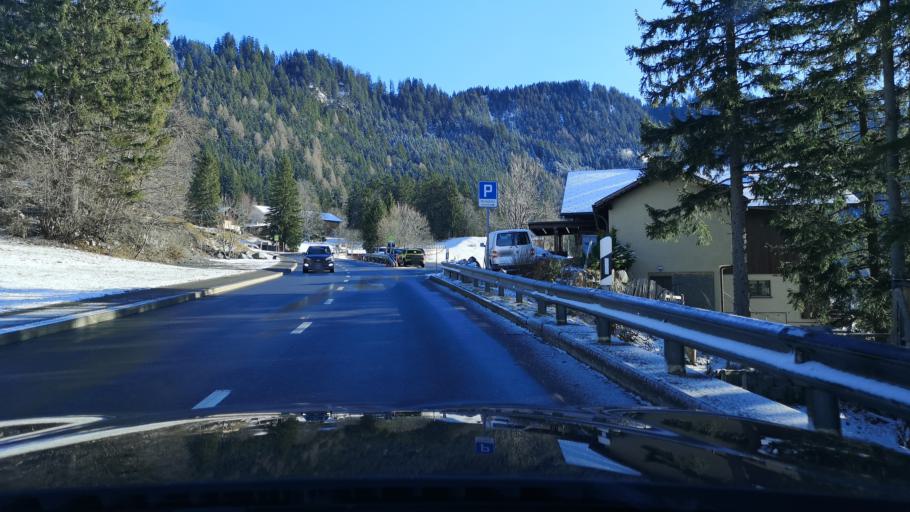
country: LI
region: Triesenberg
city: Triesenberg
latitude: 47.1204
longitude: 9.5520
